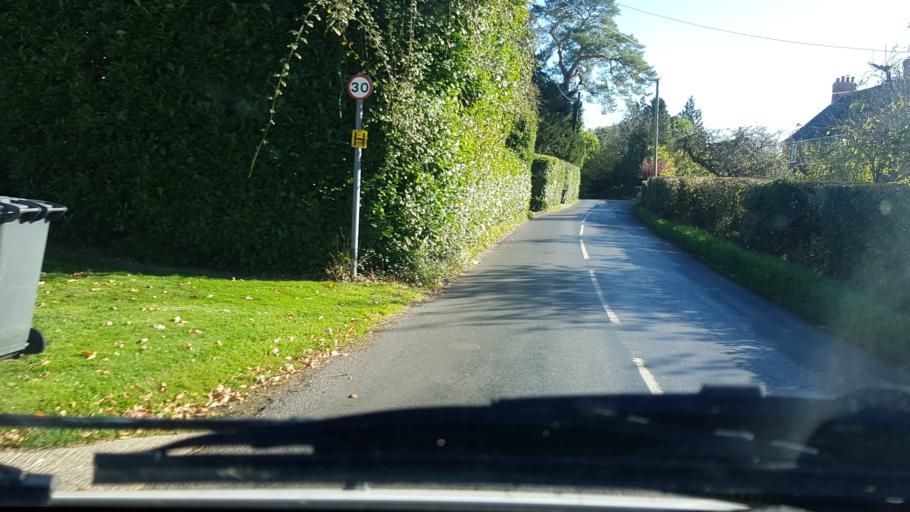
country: GB
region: England
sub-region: Surrey
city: Cranleigh
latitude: 51.1460
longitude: -0.4403
